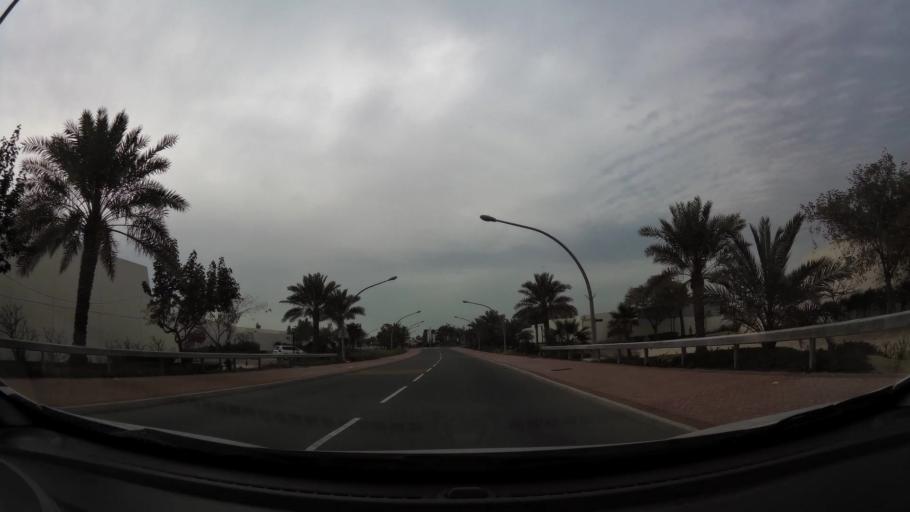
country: BH
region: Central Governorate
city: Dar Kulayb
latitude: 25.8377
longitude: 50.6151
